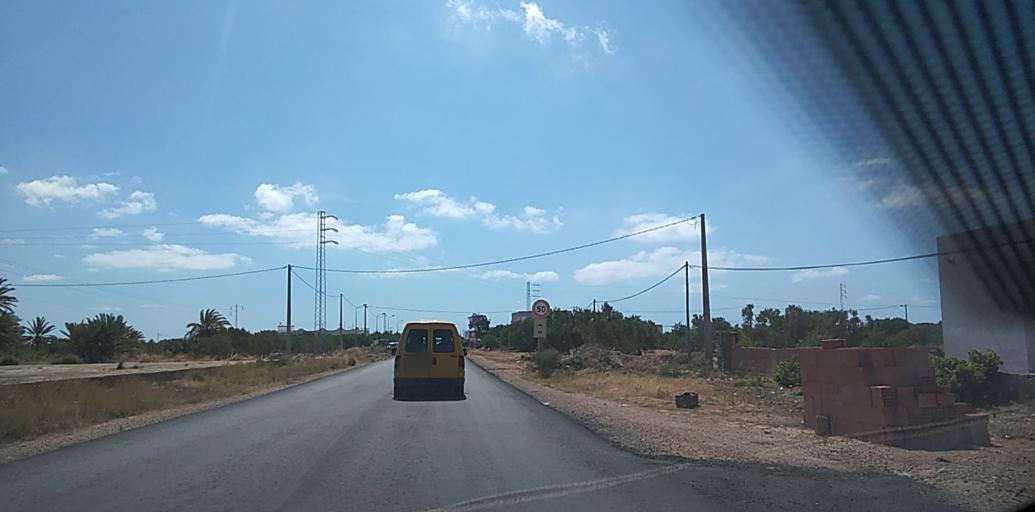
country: TN
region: Safaqis
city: Al Qarmadah
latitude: 34.6569
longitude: 11.0864
